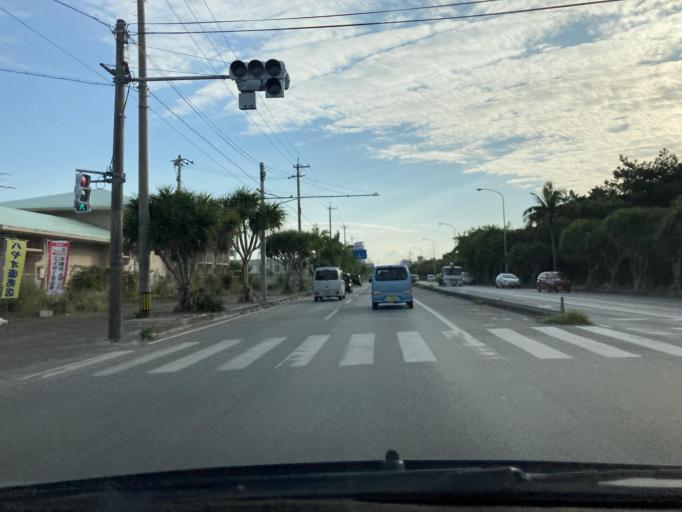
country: JP
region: Okinawa
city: Okinawa
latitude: 26.3243
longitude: 127.8338
